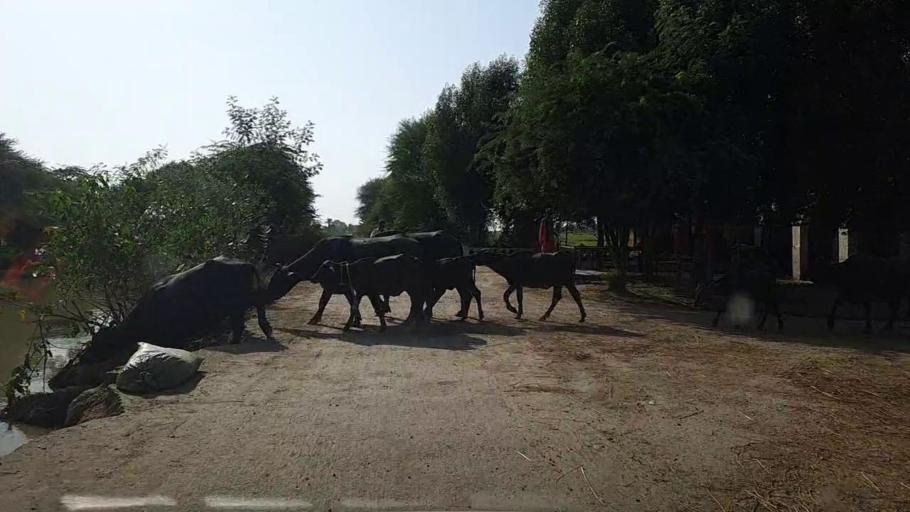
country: PK
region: Sindh
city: Kario
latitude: 24.8065
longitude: 68.5276
